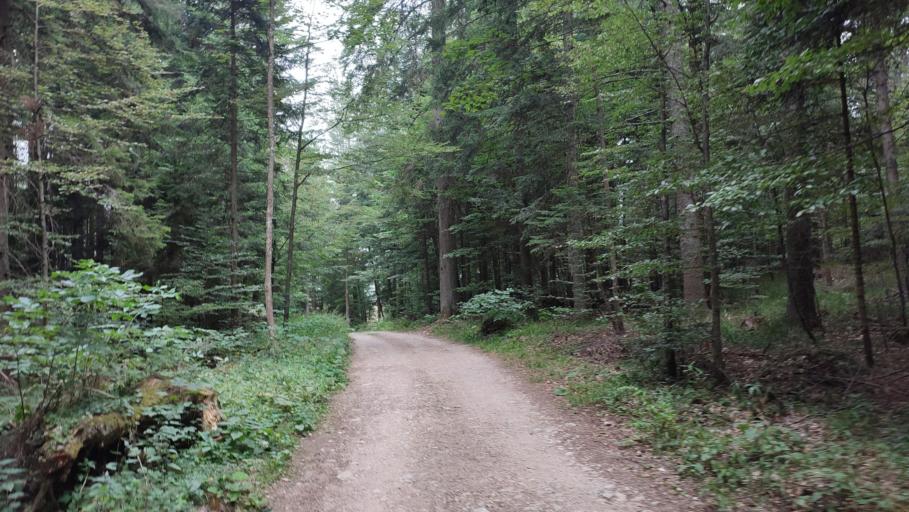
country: RS
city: Durici
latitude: 43.9268
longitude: 19.4138
